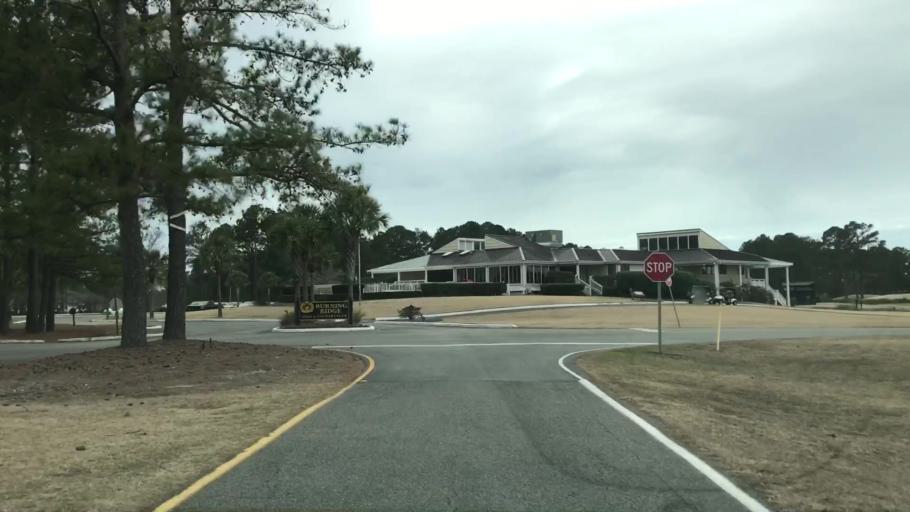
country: US
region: South Carolina
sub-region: Horry County
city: Red Hill
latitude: 33.7770
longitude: -79.0034
